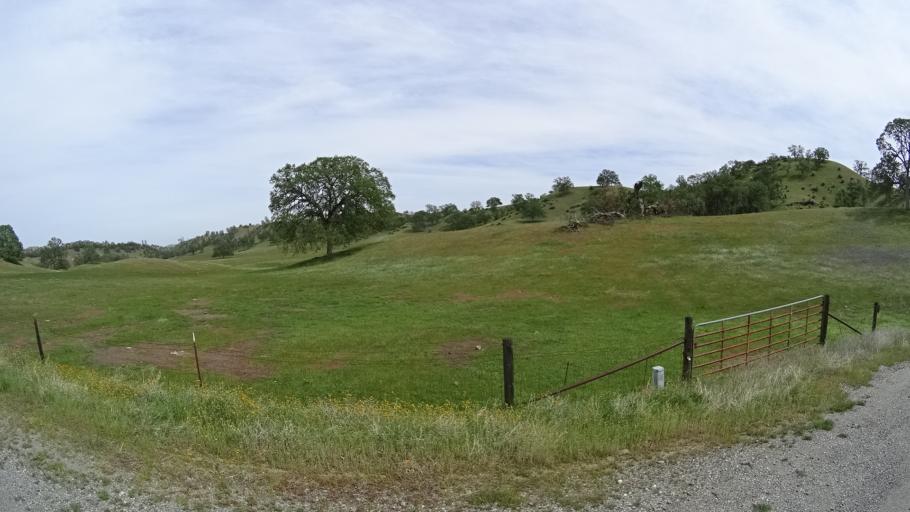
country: US
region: California
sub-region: Glenn County
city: Willows
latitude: 39.6214
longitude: -122.5925
